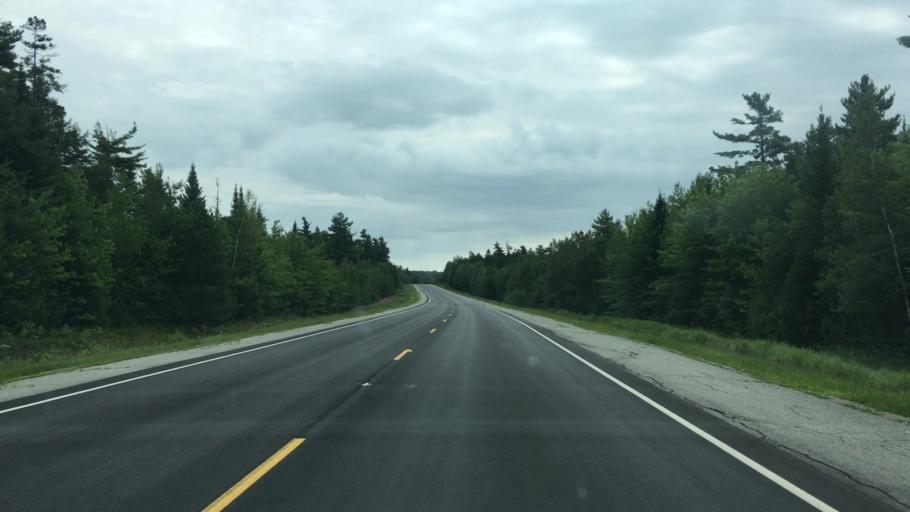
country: US
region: Maine
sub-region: Washington County
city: Addison
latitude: 44.9060
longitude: -67.8233
